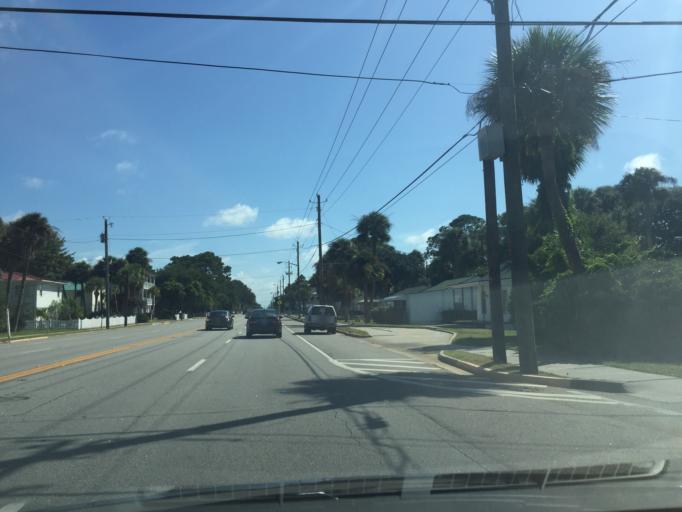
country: US
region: Georgia
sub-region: Chatham County
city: Tybee Island
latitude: 32.0066
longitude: -80.8436
